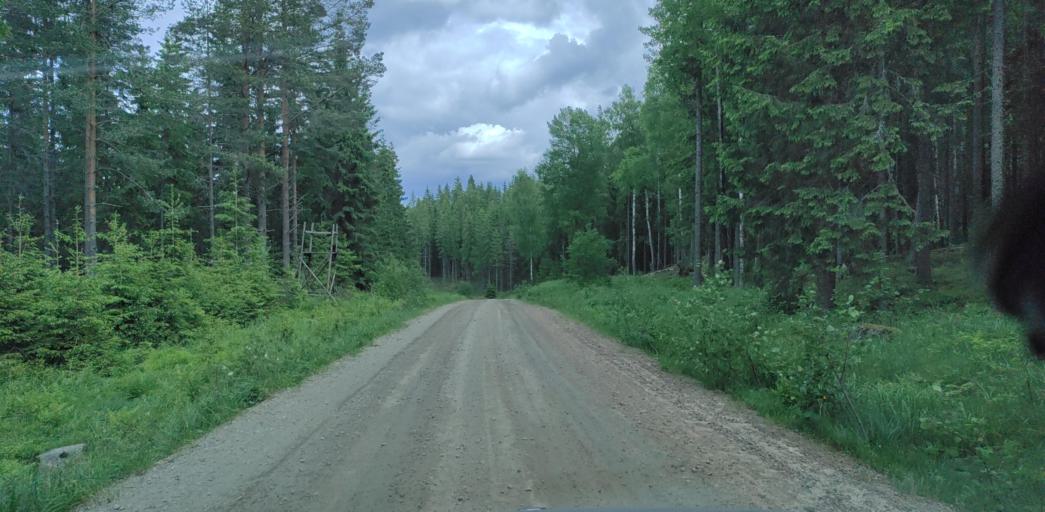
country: SE
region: Vaermland
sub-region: Munkfors Kommun
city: Munkfors
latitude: 59.9612
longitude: 13.4149
